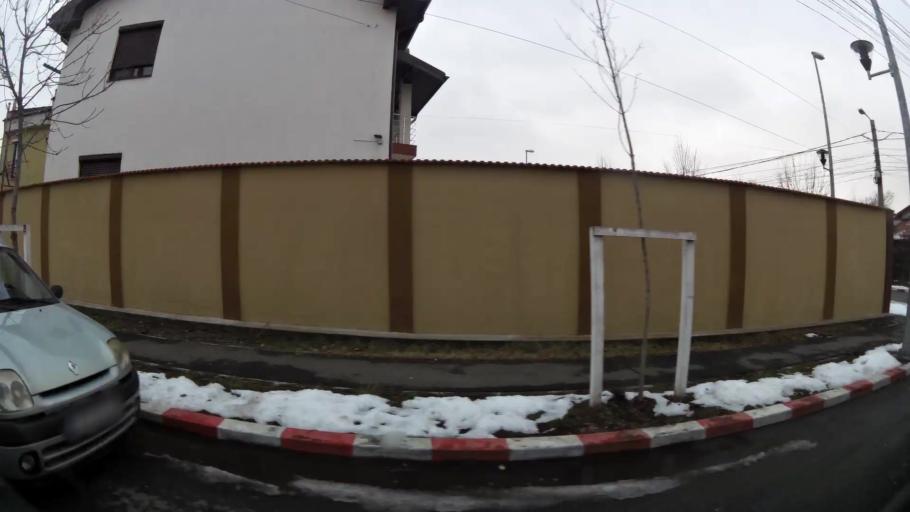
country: RO
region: Ilfov
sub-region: Voluntari City
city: Voluntari
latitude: 44.4894
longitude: 26.1768
